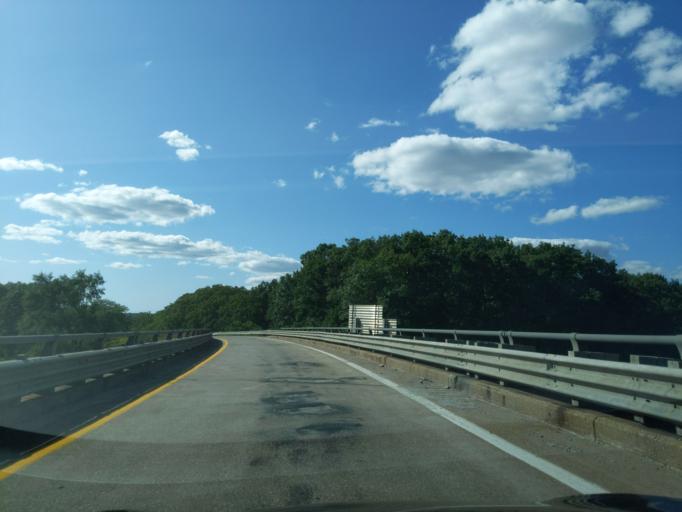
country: US
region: Michigan
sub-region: Muskegon County
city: Muskegon
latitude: 43.2573
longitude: -86.2063
